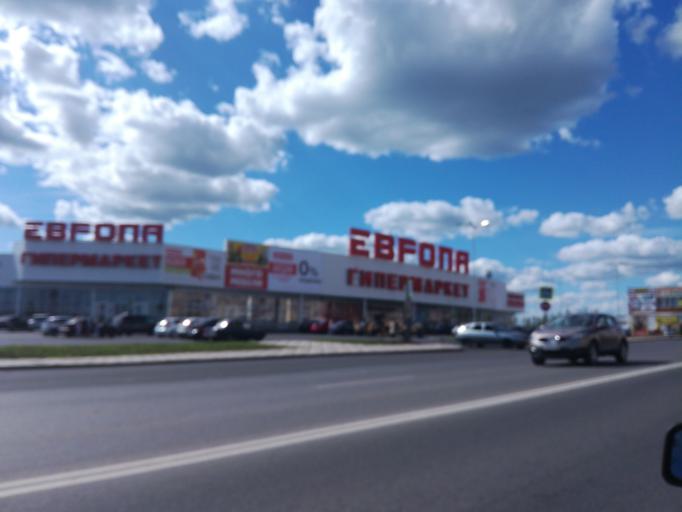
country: RU
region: Kursk
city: Kursk
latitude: 51.8038
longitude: 36.1642
